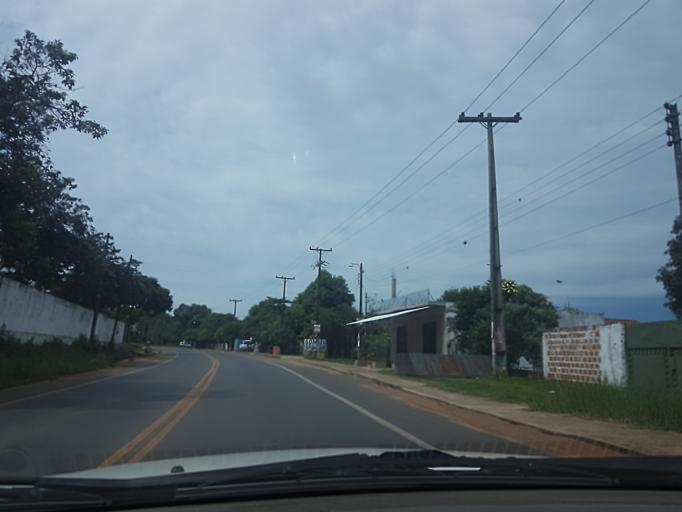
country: PY
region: Central
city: Limpio
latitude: -25.2493
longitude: -57.4585
